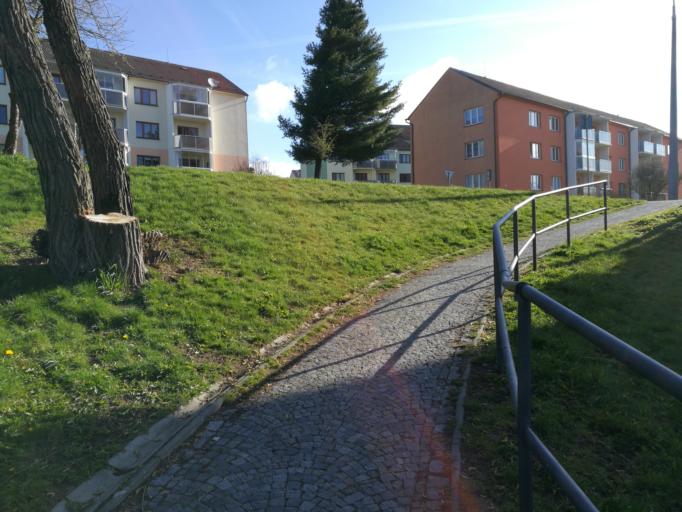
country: CZ
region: Vysocina
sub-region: Okres Zd'ar nad Sazavou
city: Zd'ar nad Sazavou
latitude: 49.5642
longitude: 15.9251
